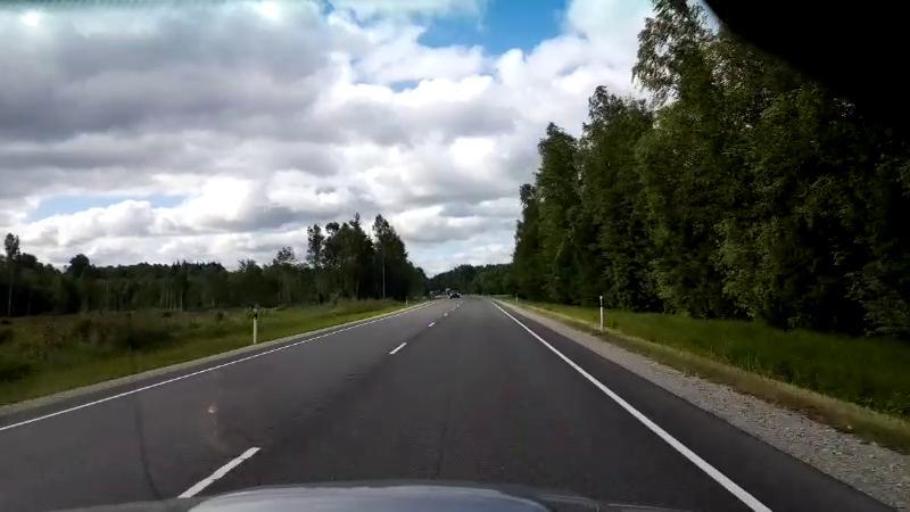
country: EE
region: Raplamaa
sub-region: Maerjamaa vald
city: Marjamaa
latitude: 58.8212
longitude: 24.4134
